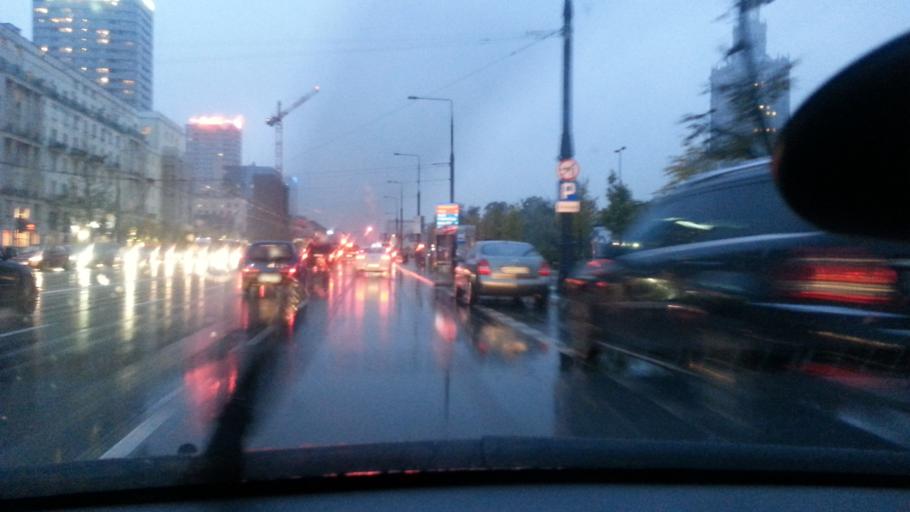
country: PL
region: Masovian Voivodeship
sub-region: Warszawa
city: Warsaw
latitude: 52.2369
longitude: 21.0074
